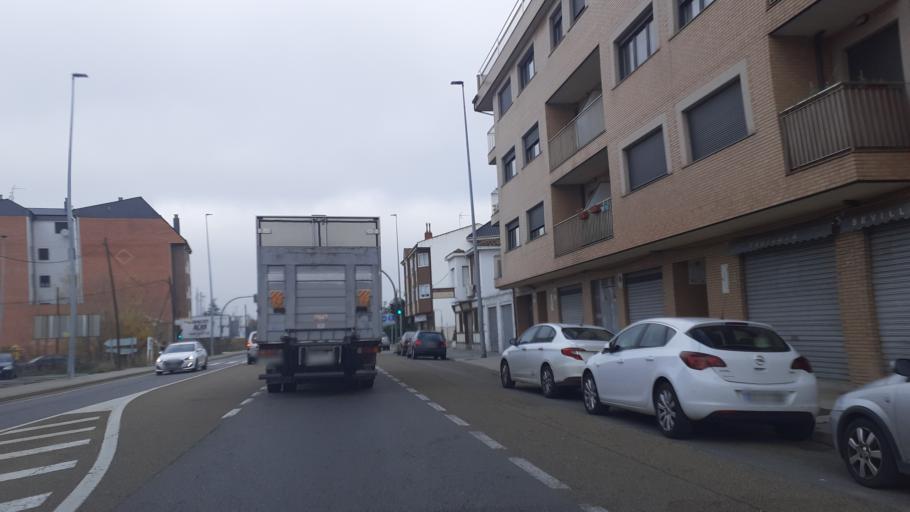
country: ES
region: Castille and Leon
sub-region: Provincia de Leon
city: Leon
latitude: 42.5646
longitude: -5.5821
